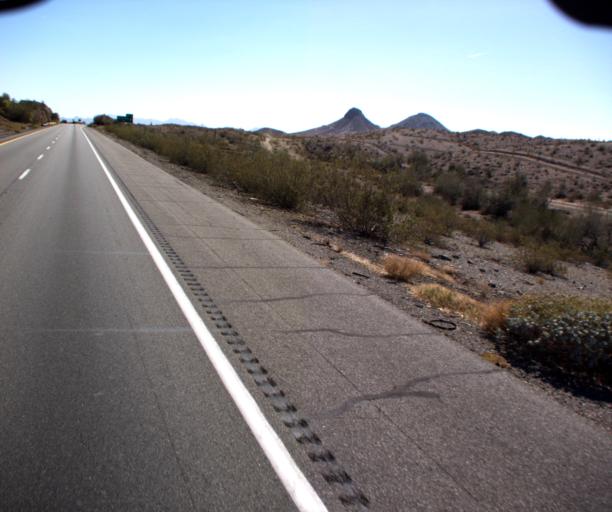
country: US
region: Arizona
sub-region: La Paz County
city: Quartzsite
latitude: 33.6471
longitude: -114.3423
